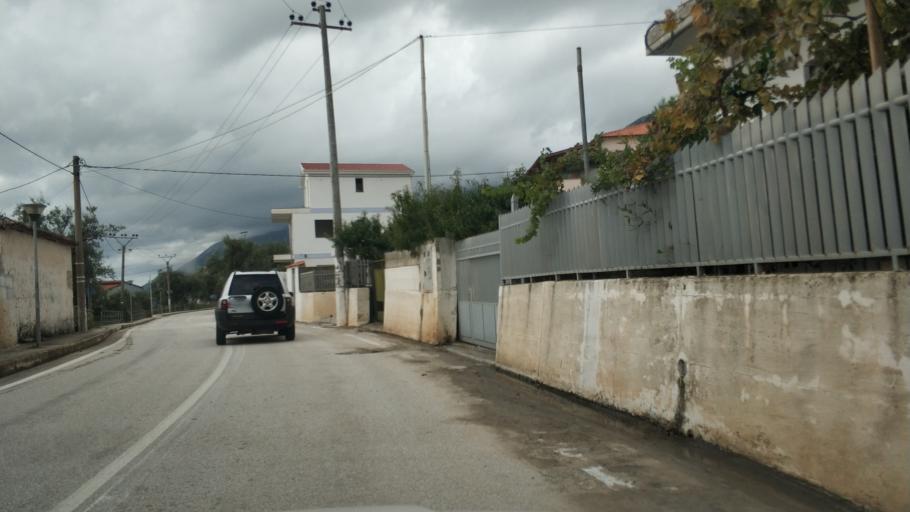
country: AL
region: Vlore
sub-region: Rrethi i Vlores
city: Vranisht
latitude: 40.1500
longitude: 19.6416
